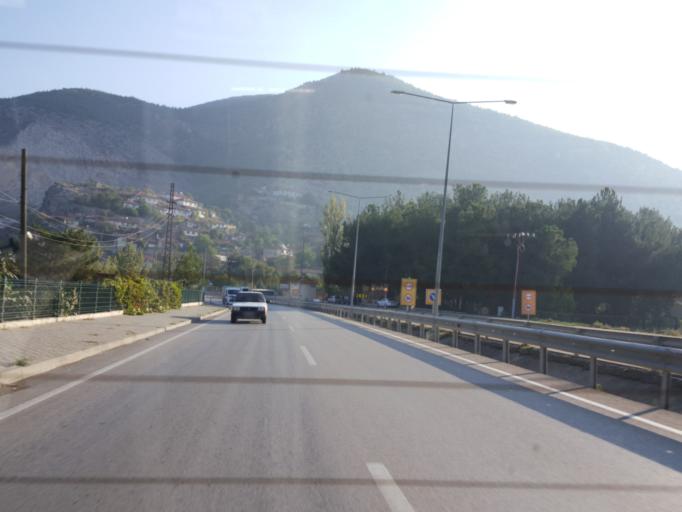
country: TR
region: Amasya
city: Amasya
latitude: 40.6189
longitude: 35.8172
